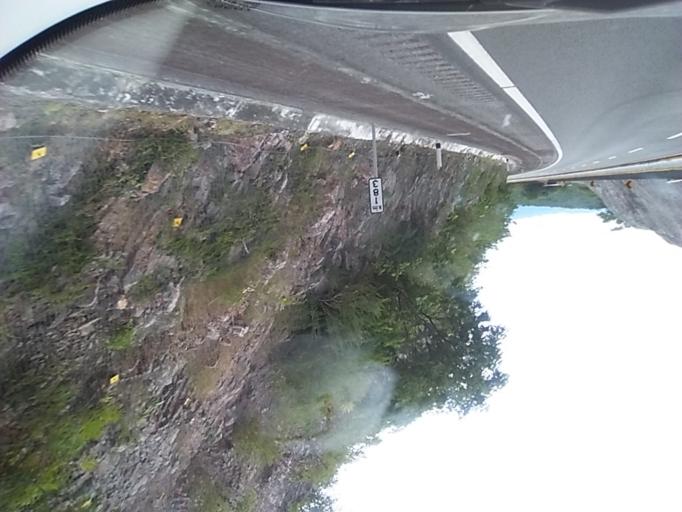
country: MX
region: Guerrero
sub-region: Huitzuco de los Figueroa
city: Ciudad de Huitzuco
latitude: 18.1892
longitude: -99.2040
